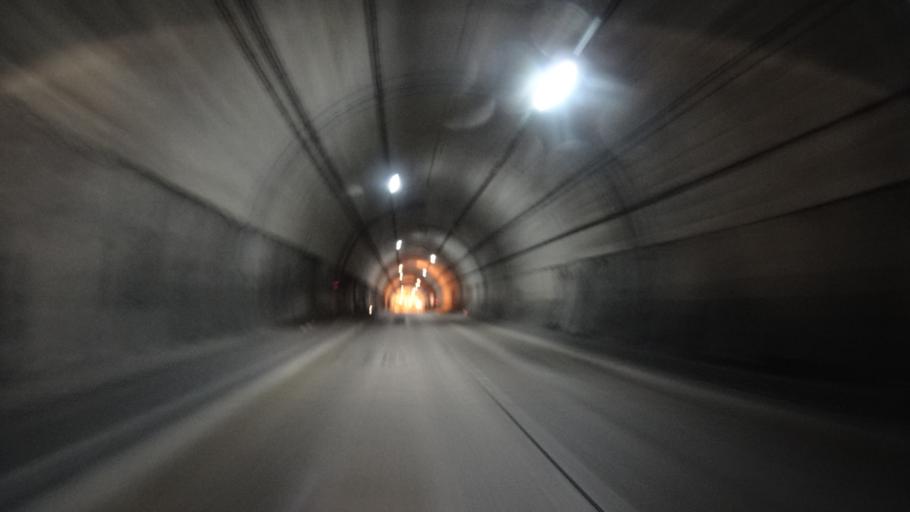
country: JP
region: Ishikawa
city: Tsurugi-asahimachi
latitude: 36.3684
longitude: 136.5866
